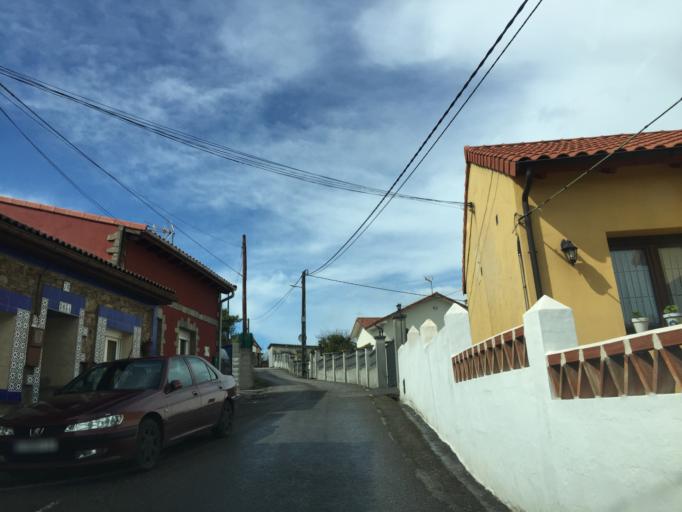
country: ES
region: Asturias
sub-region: Province of Asturias
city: Natahoyo
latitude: 43.5526
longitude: -5.7066
